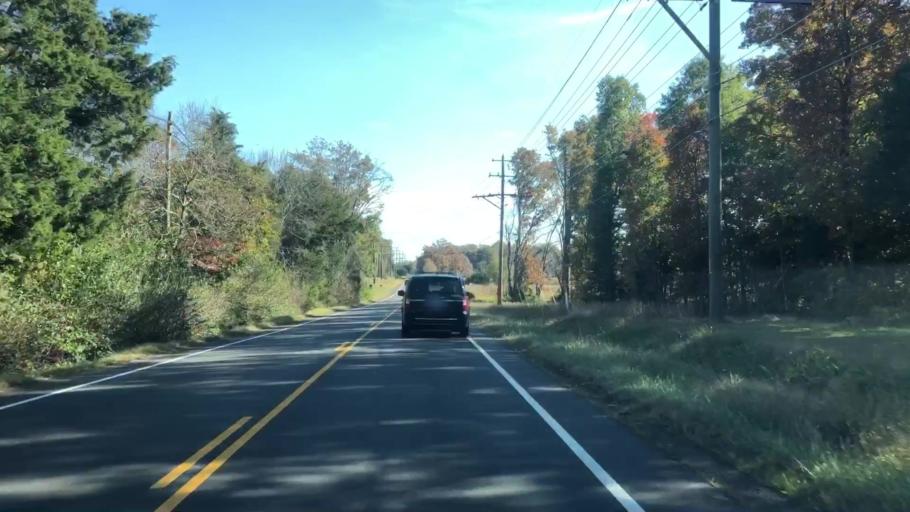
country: US
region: Virginia
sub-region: Prince William County
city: Linton Hall
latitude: 38.7450
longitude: -77.6077
